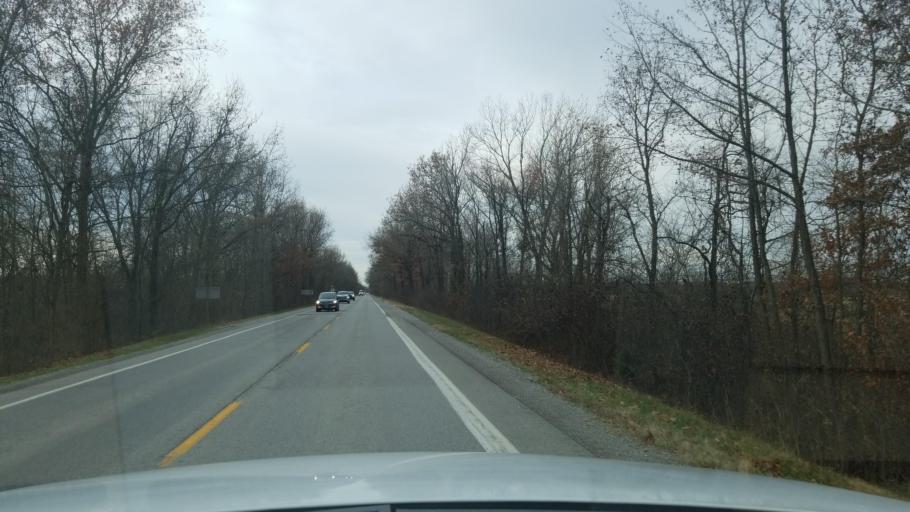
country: US
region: Illinois
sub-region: White County
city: Carmi
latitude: 37.9221
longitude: -88.1085
